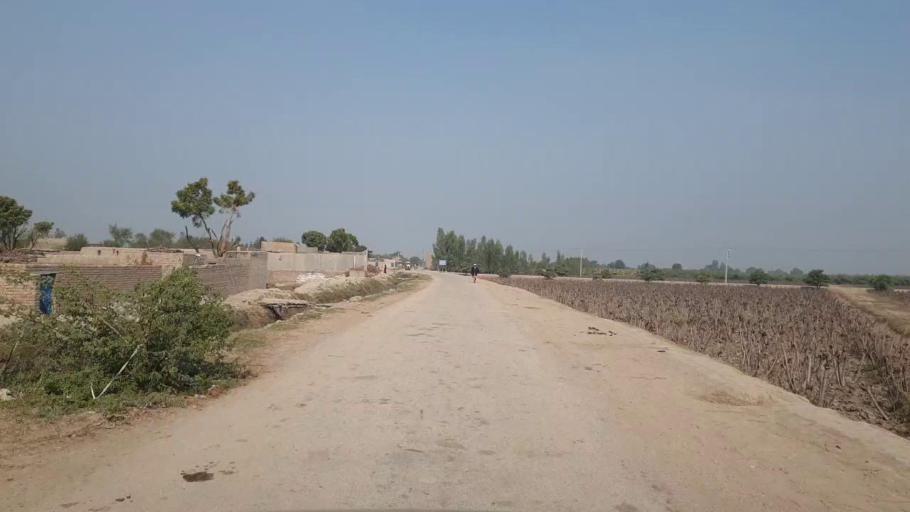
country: PK
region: Sindh
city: Bhit Shah
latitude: 25.7910
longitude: 68.4930
